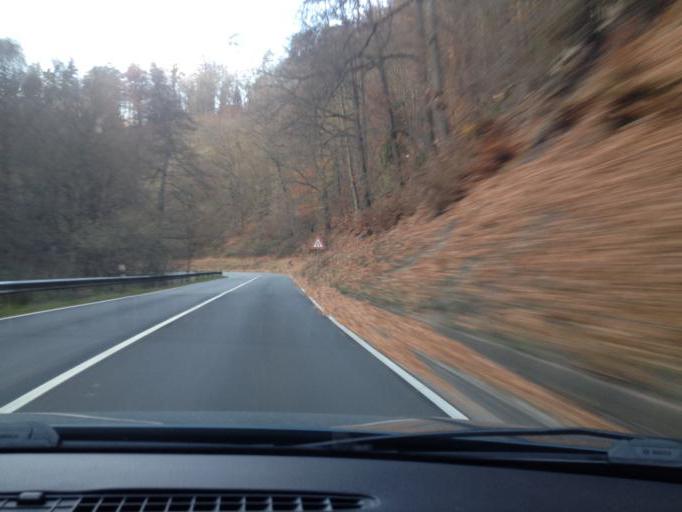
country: DE
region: Rheinland-Pfalz
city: Neidenfels
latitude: 49.3961
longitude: 8.0281
